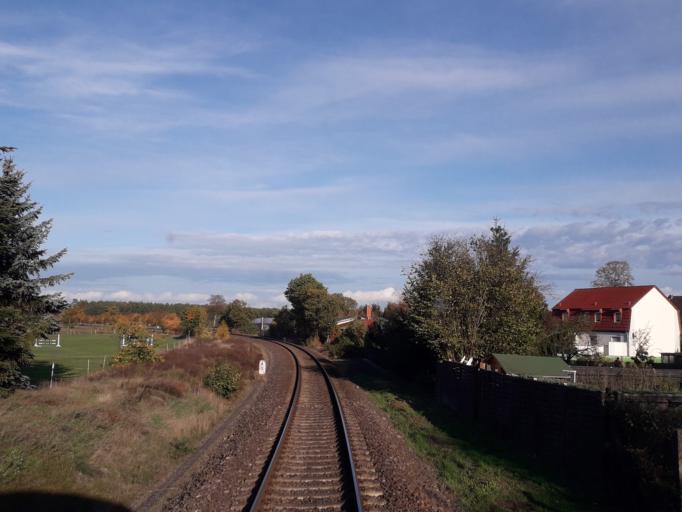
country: DE
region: Brandenburg
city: Weisen
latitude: 53.0265
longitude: 11.7916
